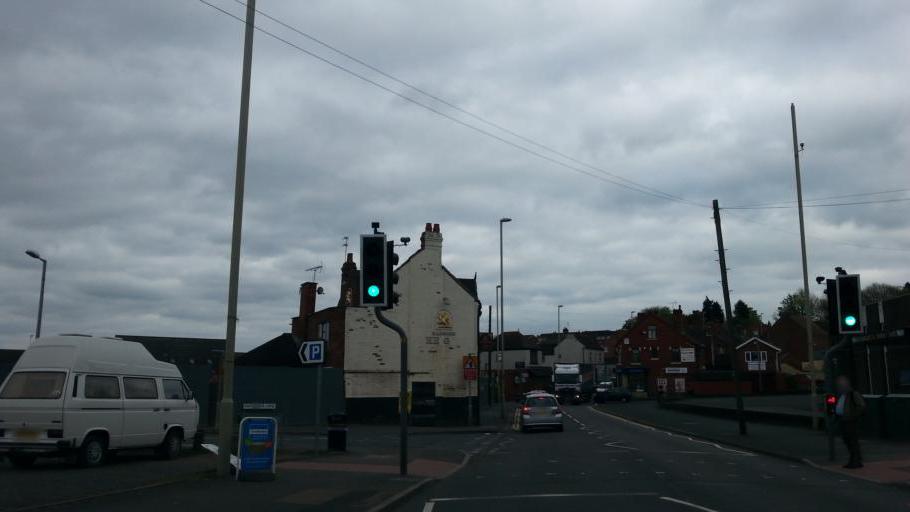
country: GB
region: England
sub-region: Sandwell
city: Cradley Heath
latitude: 52.4597
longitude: -2.0866
